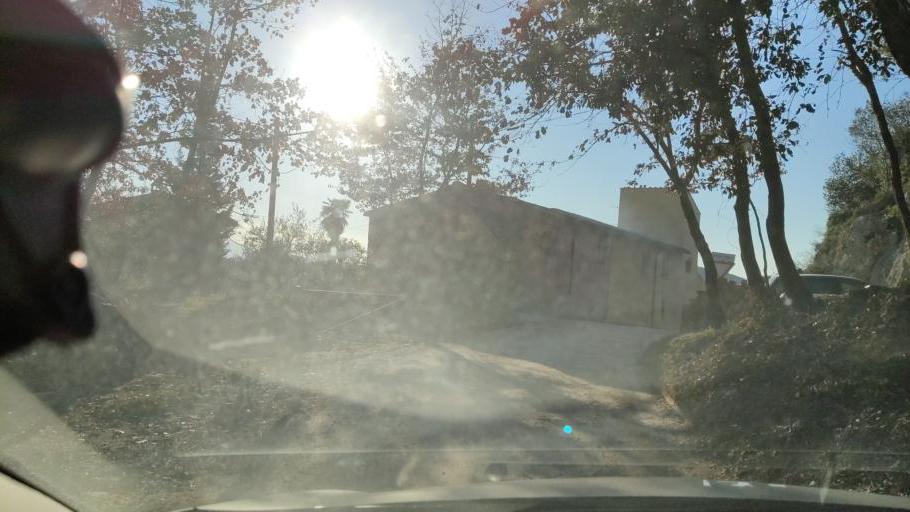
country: IT
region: Umbria
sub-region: Provincia di Terni
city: Fornole
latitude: 42.5532
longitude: 12.4442
